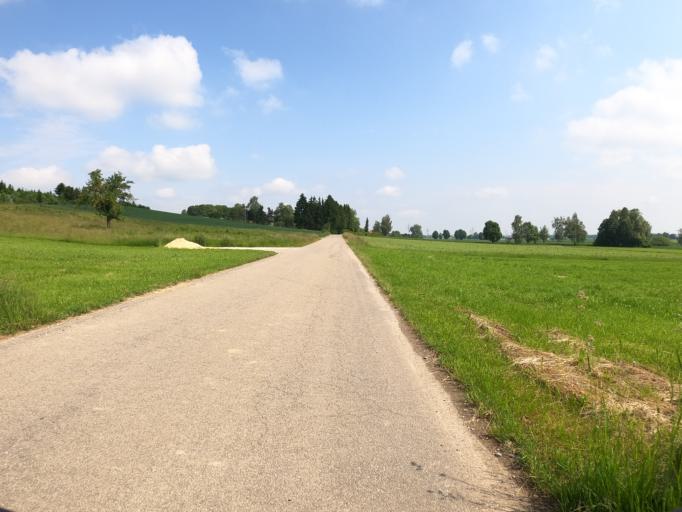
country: DE
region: Bavaria
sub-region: Swabia
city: Holzheim
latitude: 48.3548
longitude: 10.0987
